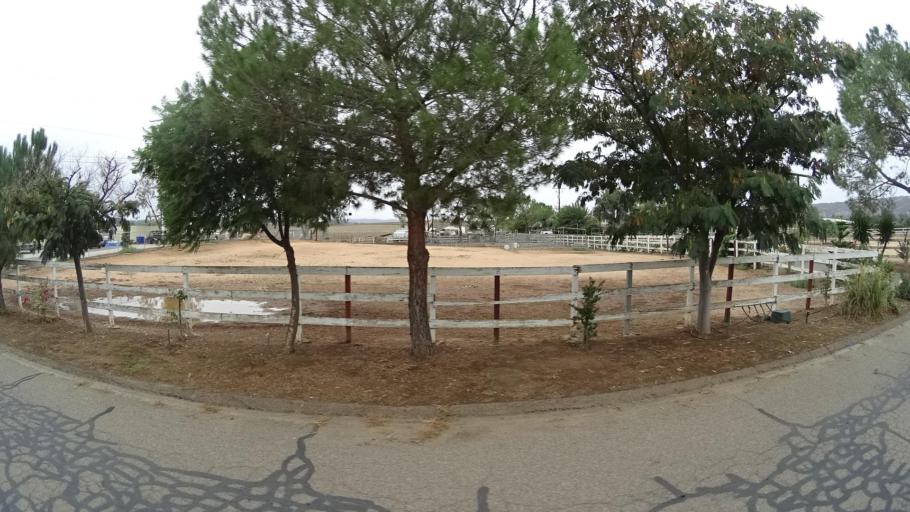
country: US
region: California
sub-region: San Diego County
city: Ramona
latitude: 33.0696
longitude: -116.8632
